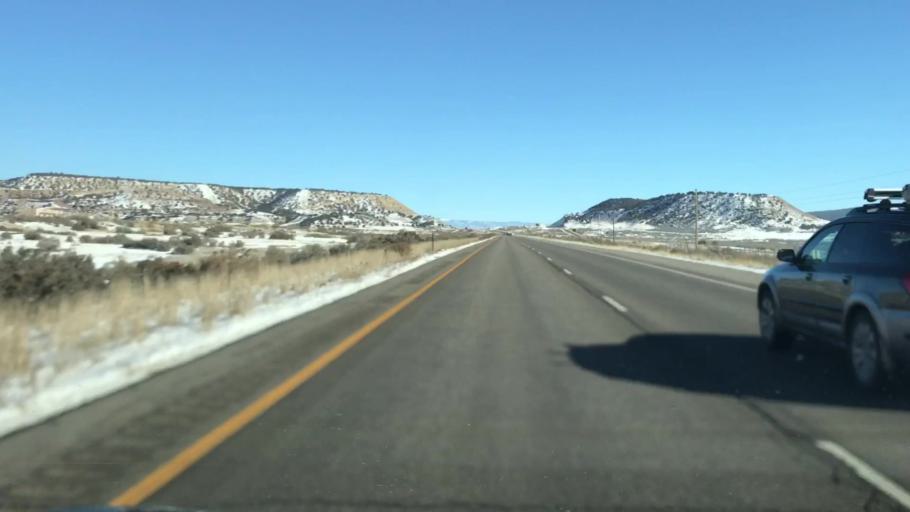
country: US
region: Colorado
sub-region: Garfield County
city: Rifle
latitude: 39.5030
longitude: -107.9004
